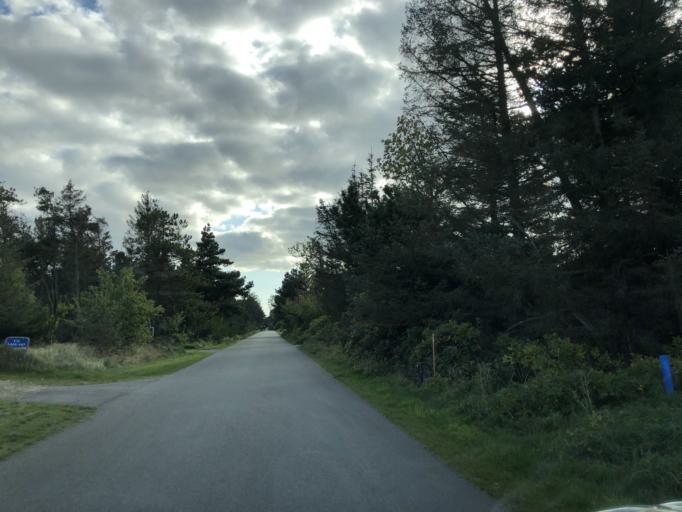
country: DK
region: Central Jutland
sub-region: Holstebro Kommune
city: Ulfborg
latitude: 56.3317
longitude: 8.1601
